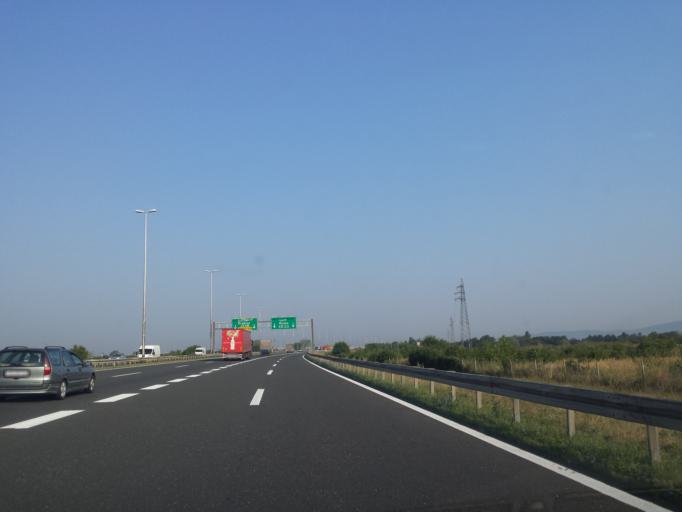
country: HR
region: Grad Zagreb
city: Zadvorsko
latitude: 45.7528
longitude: 15.9079
